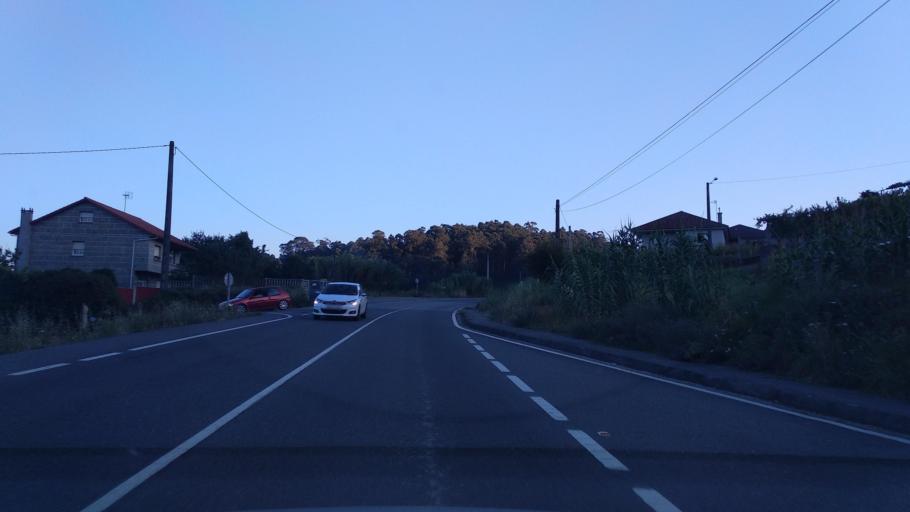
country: ES
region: Galicia
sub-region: Provincia de Pontevedra
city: Marin
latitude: 42.3510
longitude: -8.6419
